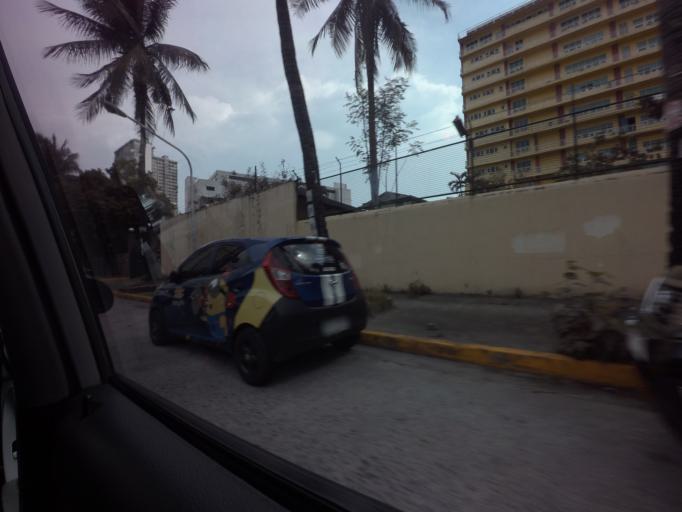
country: PH
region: Metro Manila
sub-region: San Juan
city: San Juan
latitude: 14.6041
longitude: 121.0128
